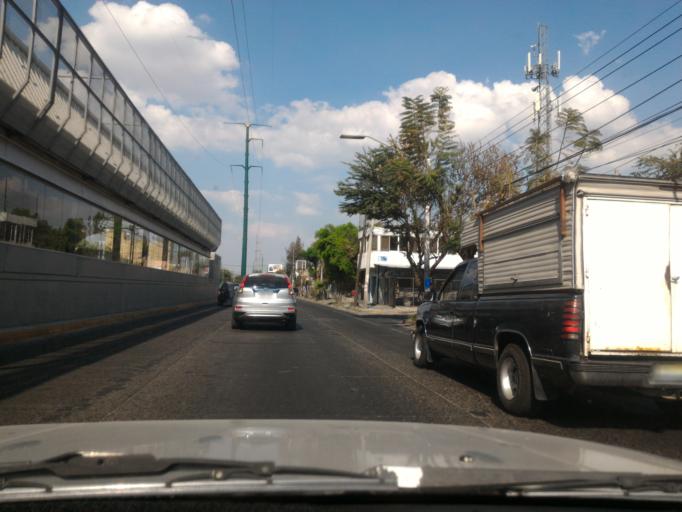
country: MX
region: Jalisco
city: Guadalajara
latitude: 20.6325
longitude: -103.3807
